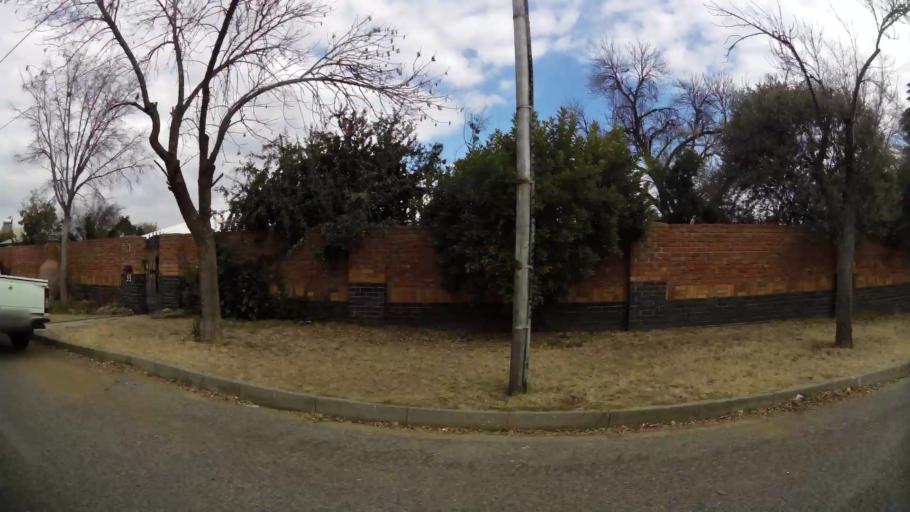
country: ZA
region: Orange Free State
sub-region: Fezile Dabi District Municipality
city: Kroonstad
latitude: -27.6494
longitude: 27.2329
